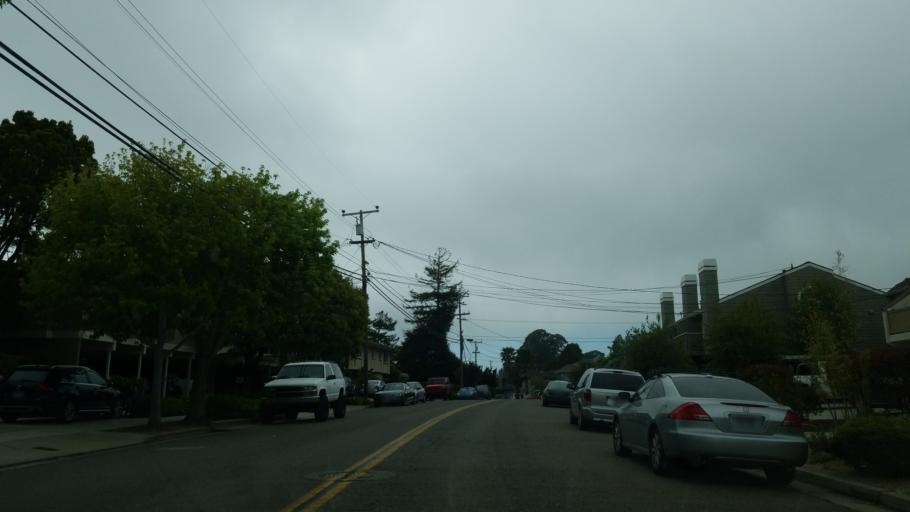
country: US
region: California
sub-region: Santa Cruz County
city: Seacliff
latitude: 36.9763
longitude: -121.9153
